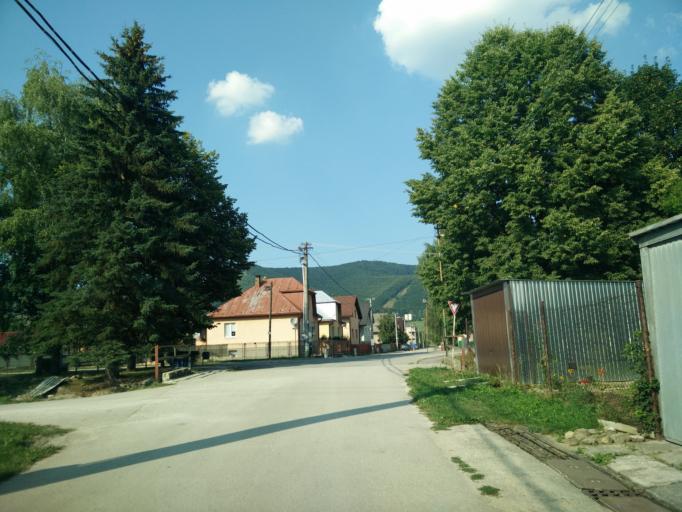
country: SK
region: Zilinsky
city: Rajec
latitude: 49.1190
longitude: 18.6507
